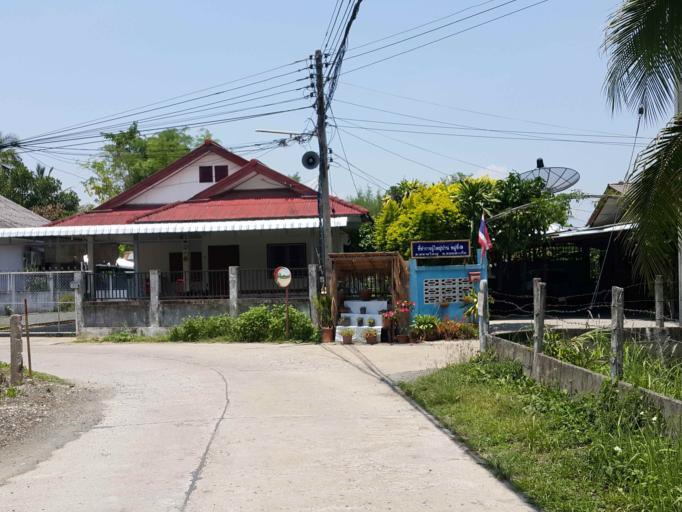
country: TH
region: Chiang Mai
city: San Kamphaeng
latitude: 18.8196
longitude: 99.1147
